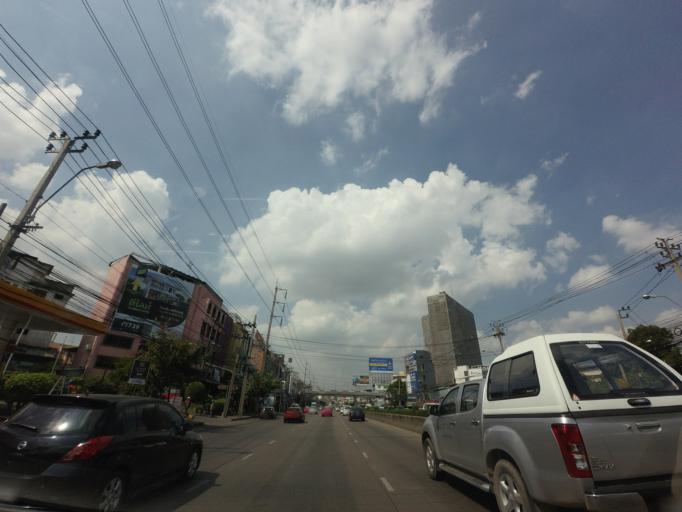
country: TH
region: Bangkok
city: Chatuchak
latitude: 13.8541
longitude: 100.5496
